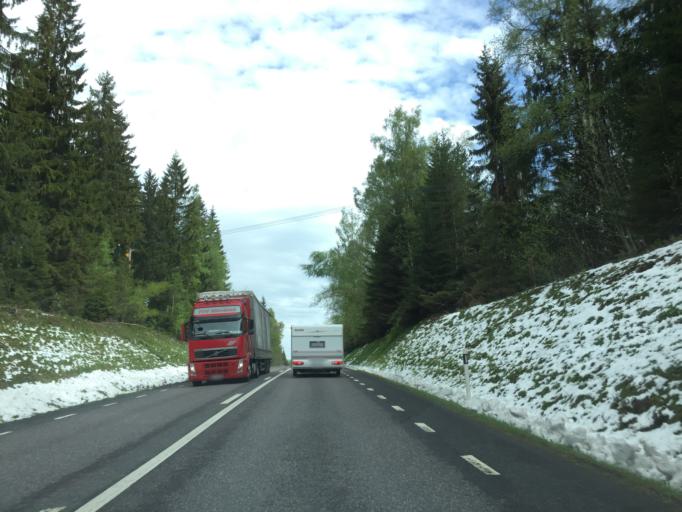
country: SE
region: Dalarna
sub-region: Ludvika Kommun
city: Ludvika
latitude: 60.1156
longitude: 15.1128
